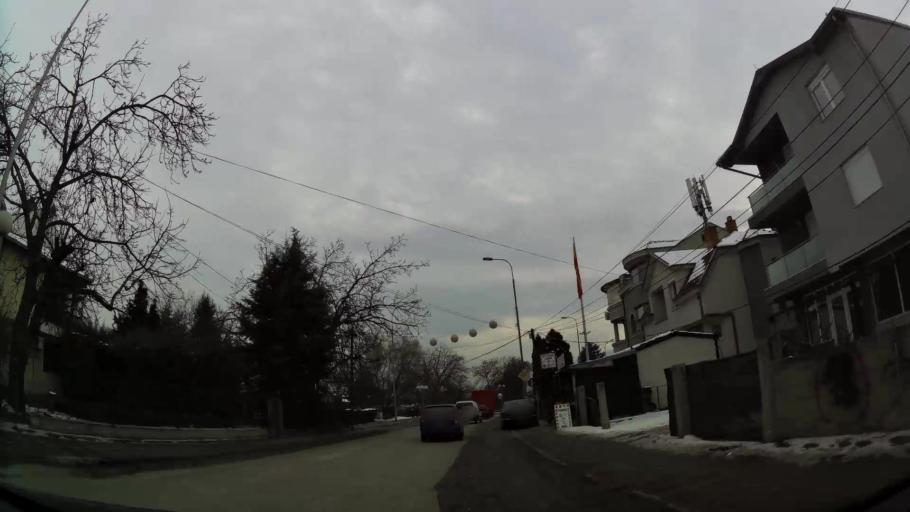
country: MK
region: Butel
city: Butel
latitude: 42.0355
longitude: 21.4463
